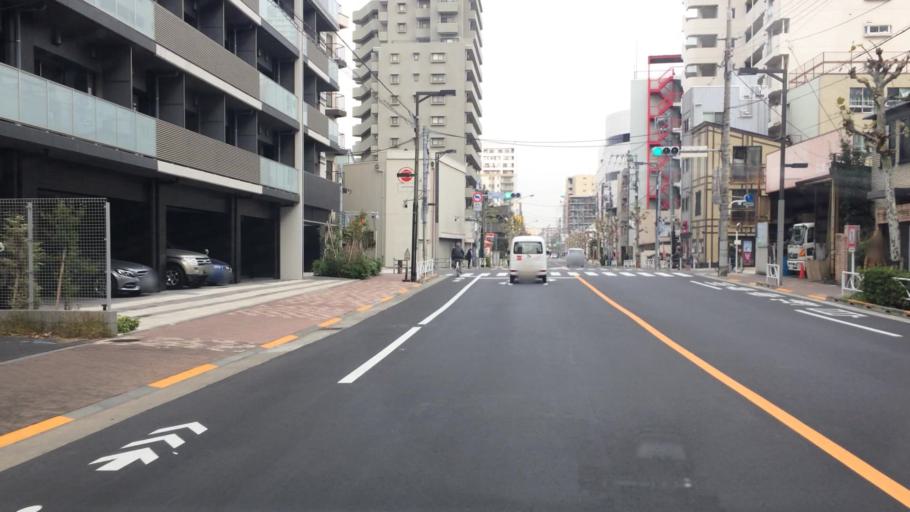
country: JP
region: Tokyo
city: Urayasu
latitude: 35.7133
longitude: 139.8123
